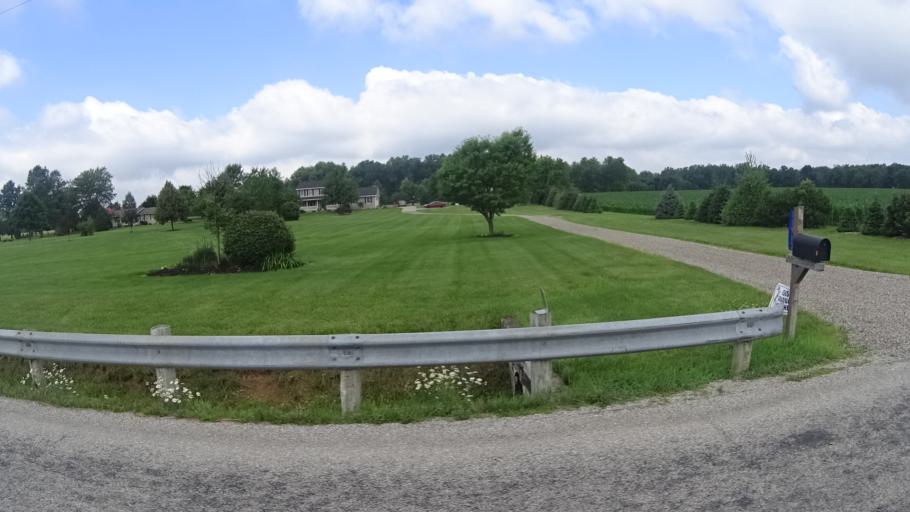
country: US
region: Ohio
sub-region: Huron County
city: Wakeman
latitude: 41.3160
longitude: -82.4509
